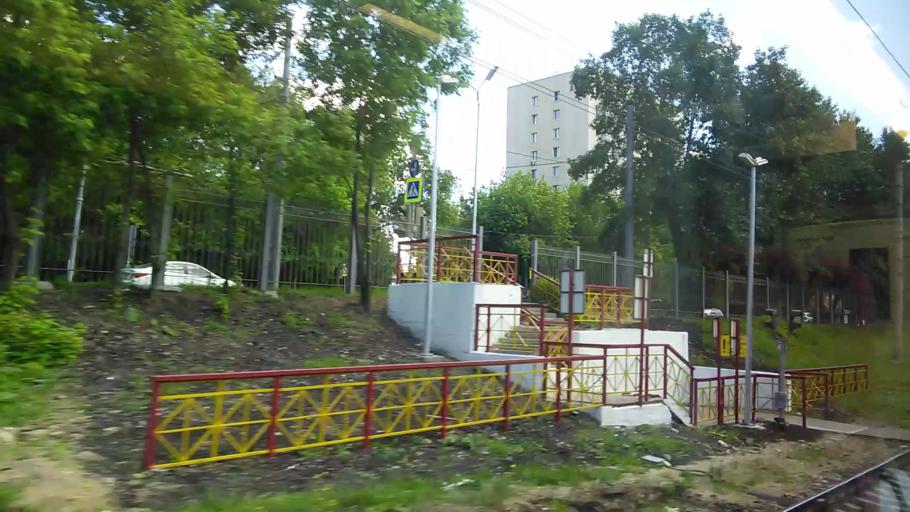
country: RU
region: Moscow
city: Mar'ina Roshcha
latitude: 55.7855
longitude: 37.5872
